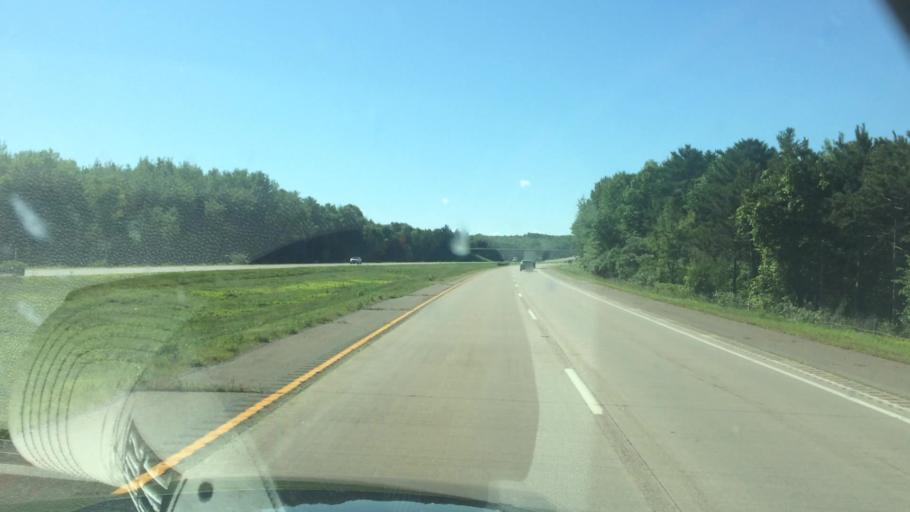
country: US
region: Wisconsin
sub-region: Marathon County
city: Mosinee
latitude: 44.7178
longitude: -89.6643
